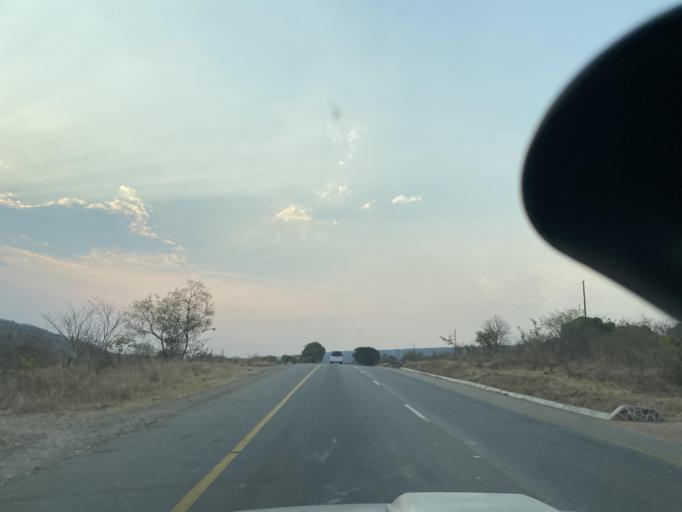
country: ZM
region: Lusaka
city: Kafue
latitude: -15.9045
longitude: 28.3493
